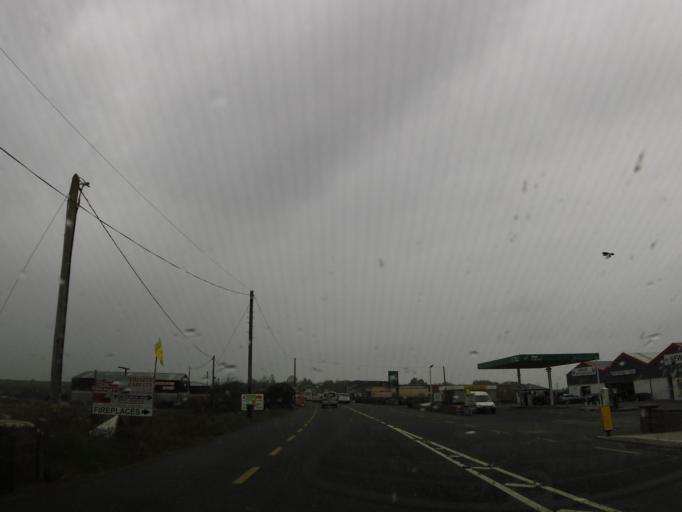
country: IE
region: Connaught
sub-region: County Galway
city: Tuam
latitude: 53.5076
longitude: -8.8753
